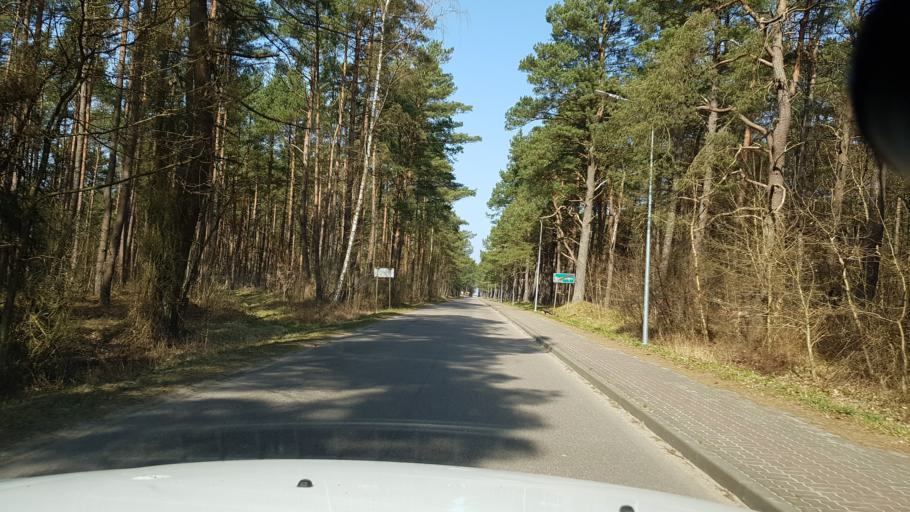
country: PL
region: West Pomeranian Voivodeship
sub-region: Powiat slawienski
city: Darlowo
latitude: 54.5230
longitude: 16.5114
